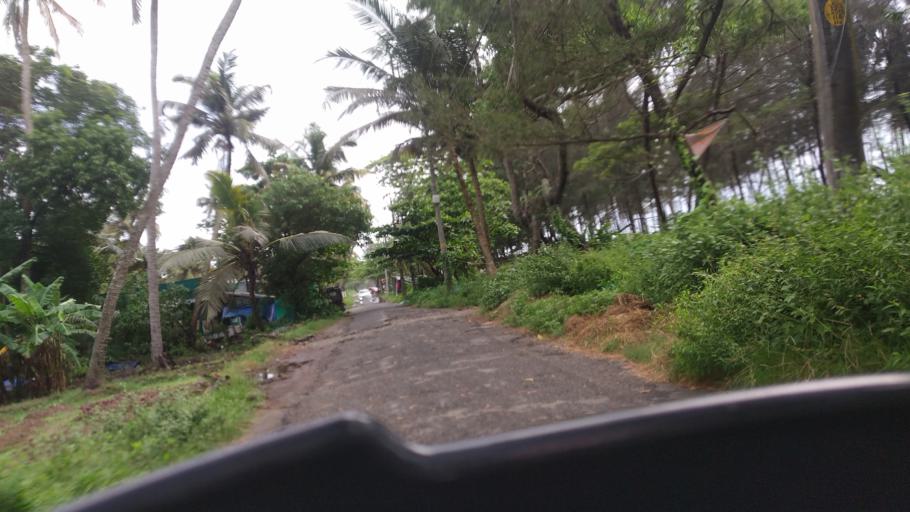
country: IN
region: Kerala
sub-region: Ernakulam
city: Elur
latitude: 10.1112
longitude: 76.1874
